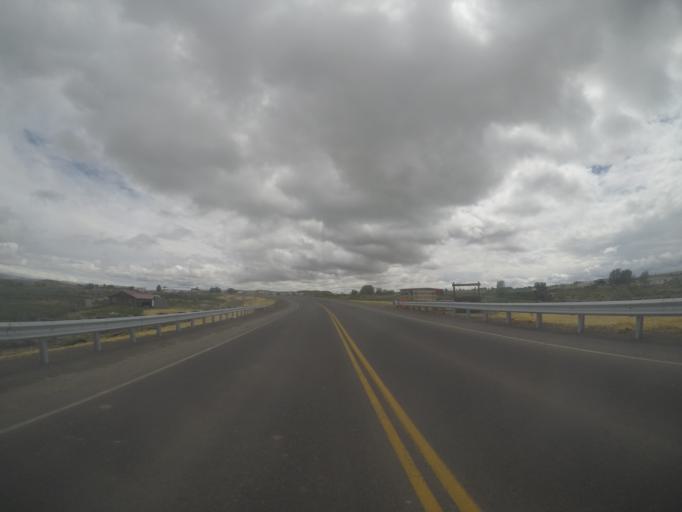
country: US
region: Wyoming
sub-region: Big Horn County
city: Lovell
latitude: 44.8471
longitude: -108.4445
